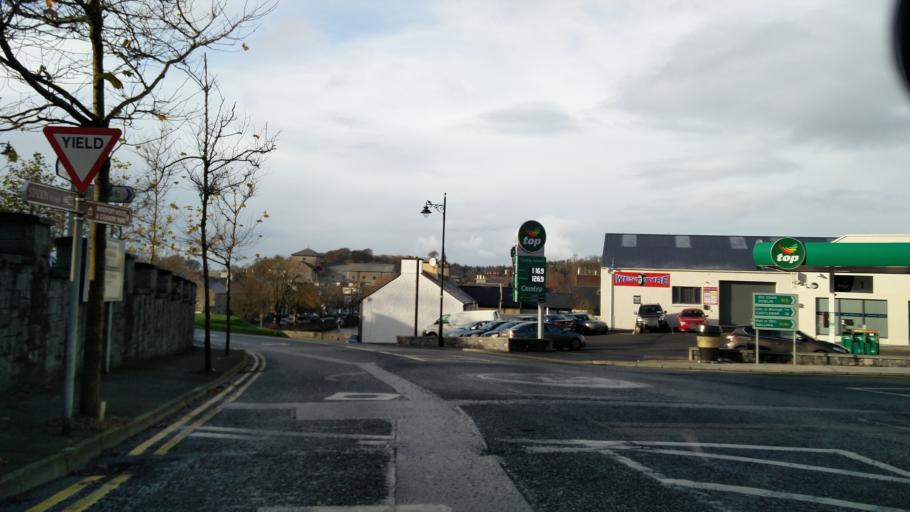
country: IE
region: Connaught
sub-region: Maigh Eo
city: Westport
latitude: 53.7990
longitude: -9.5170
